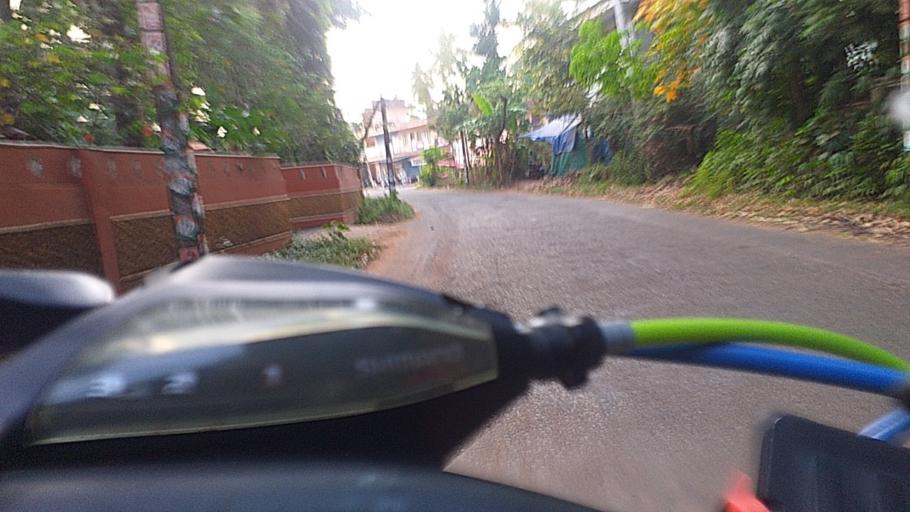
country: IN
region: Kerala
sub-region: Thrissur District
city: Kunnamkulam
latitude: 10.7454
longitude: 76.0353
